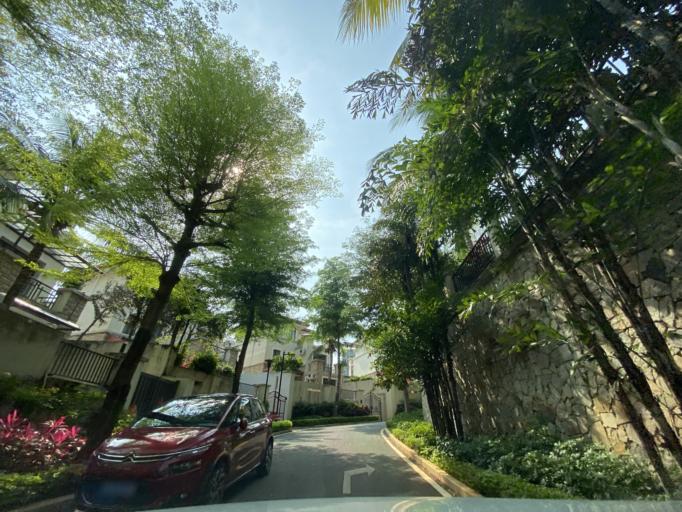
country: CN
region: Hainan
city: Yingzhou
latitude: 18.4093
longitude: 109.8439
